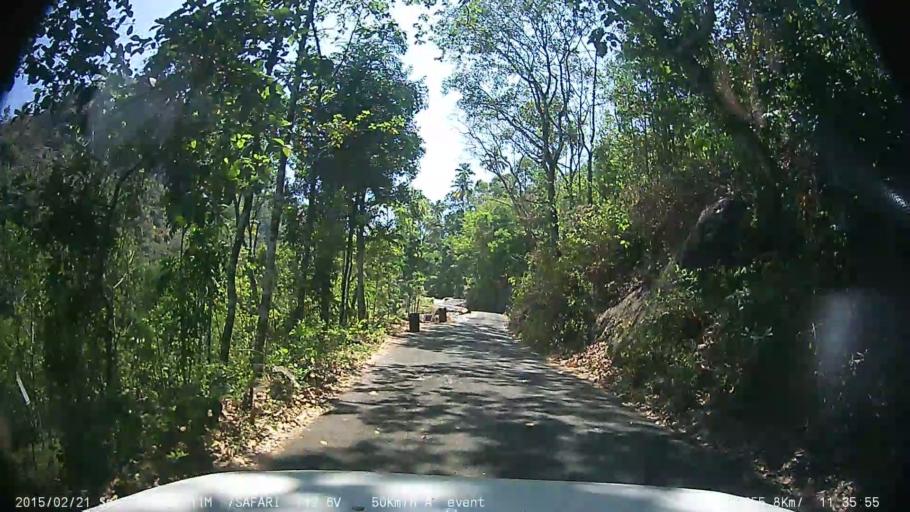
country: IN
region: Kerala
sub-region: Kottayam
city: Lalam
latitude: 9.8156
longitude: 76.7247
